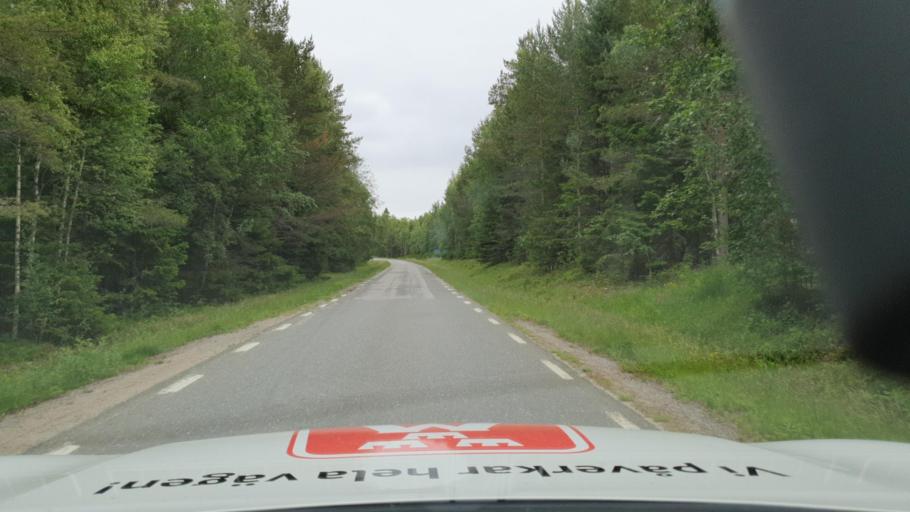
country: SE
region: Vaesterbotten
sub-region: Nordmalings Kommun
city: Nordmaling
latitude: 63.4282
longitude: 19.4938
